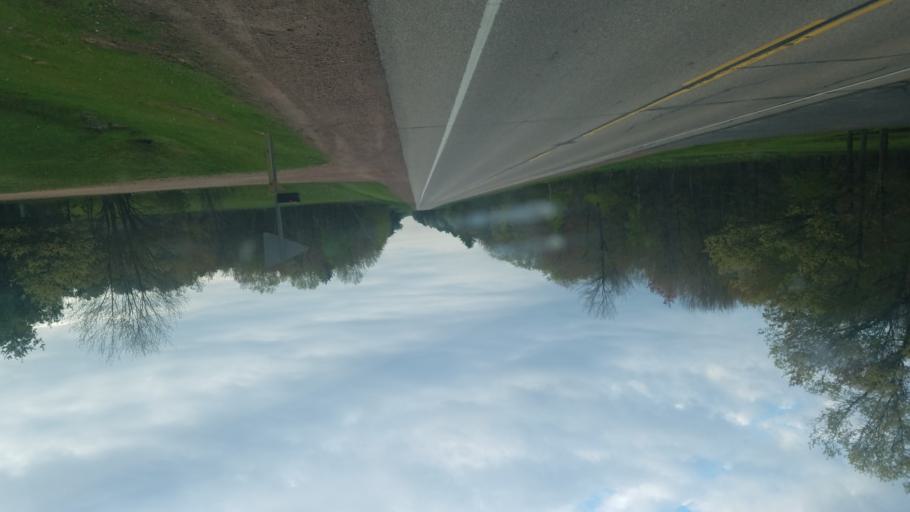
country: US
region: Wisconsin
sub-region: Wood County
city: Nekoosa
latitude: 44.3111
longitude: -90.1109
